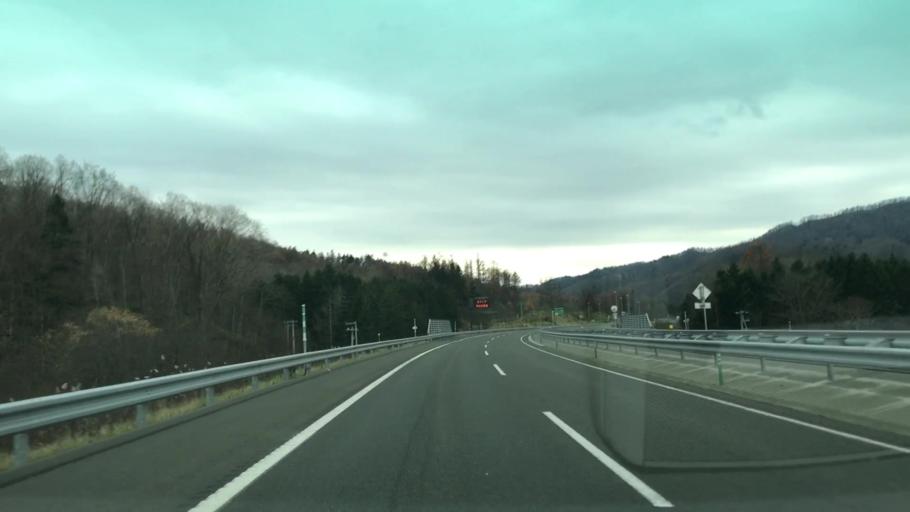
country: JP
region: Hokkaido
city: Shimo-furano
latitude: 42.9233
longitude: 142.2020
